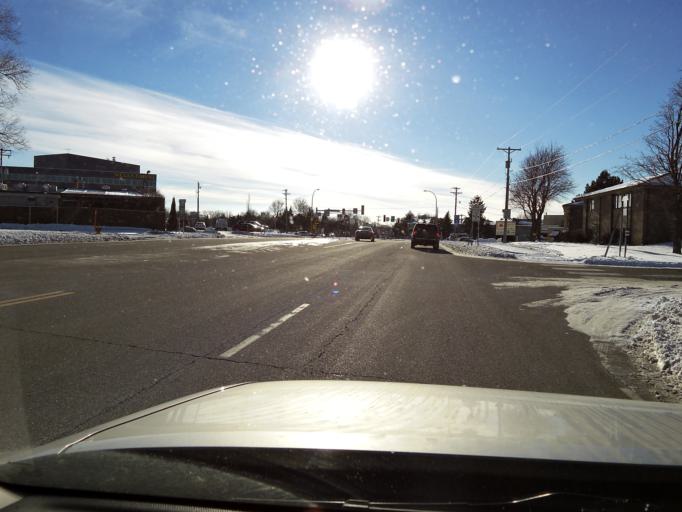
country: US
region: Minnesota
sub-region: Ramsey County
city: Maplewood
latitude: 44.9640
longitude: -93.0038
